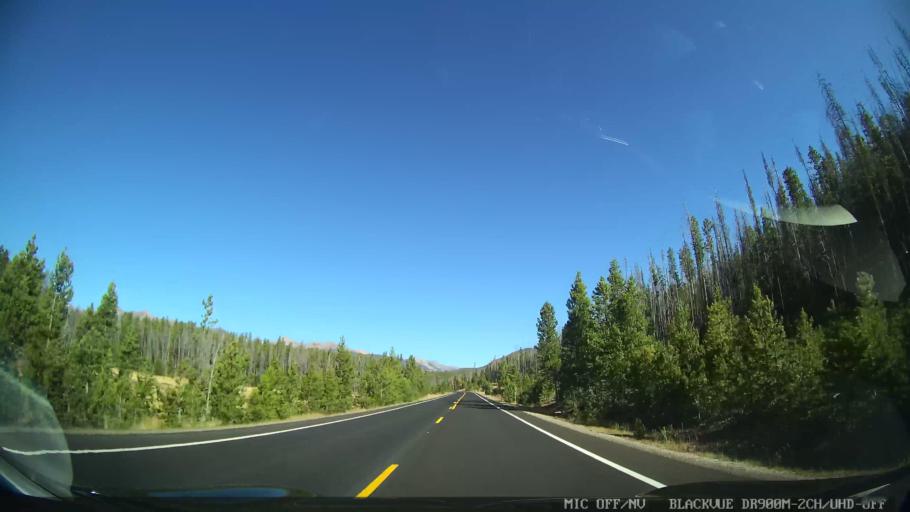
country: US
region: Colorado
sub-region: Grand County
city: Granby
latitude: 40.3122
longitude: -105.8426
